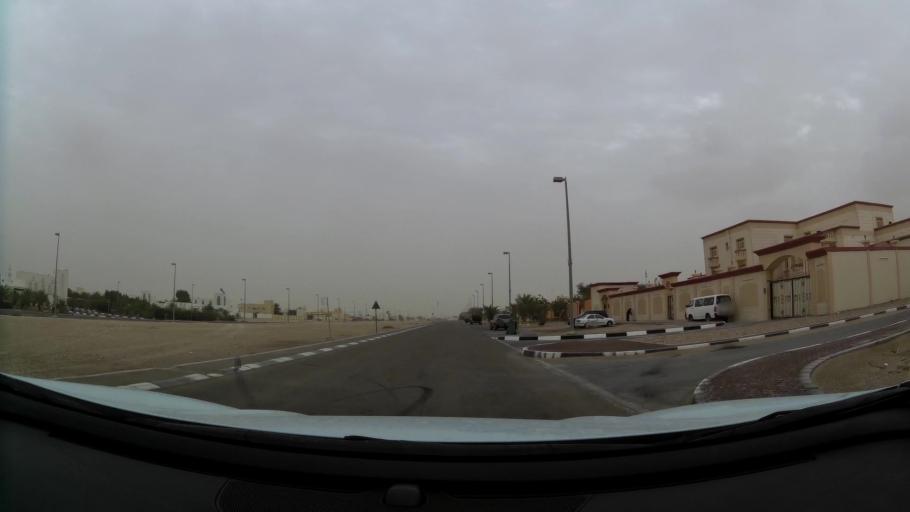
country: AE
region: Abu Dhabi
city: Abu Dhabi
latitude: 24.4241
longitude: 54.7349
